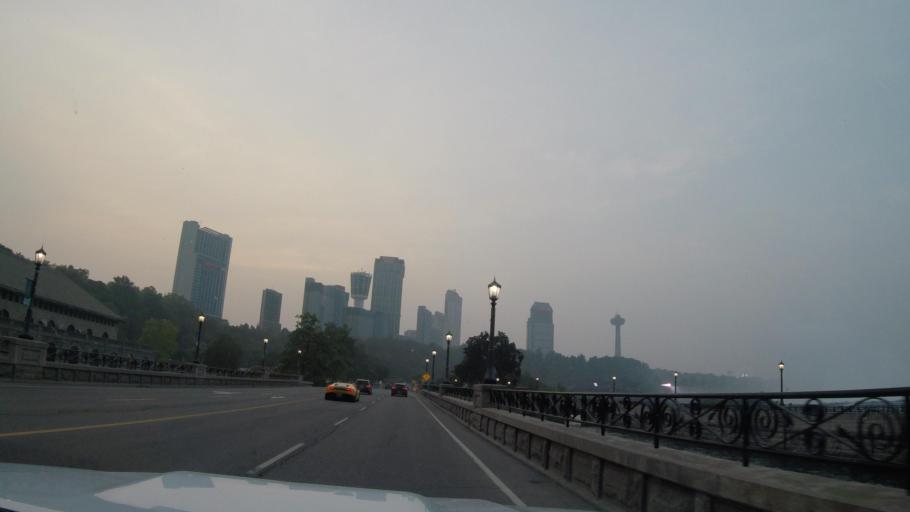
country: CA
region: Ontario
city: Niagara Falls
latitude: 43.0746
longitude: -79.0778
